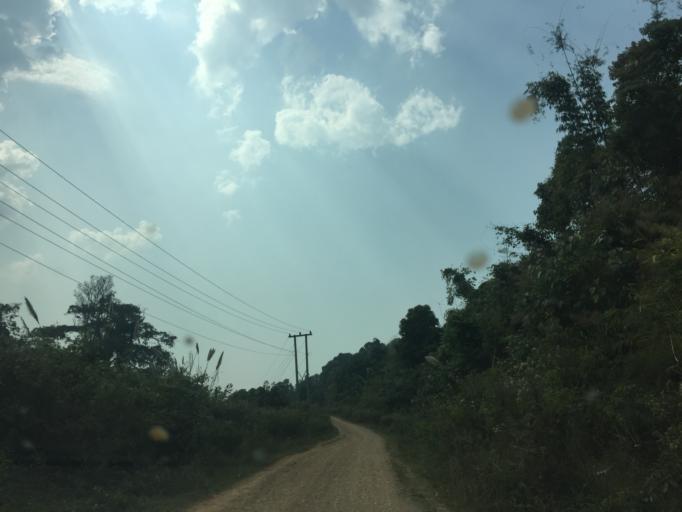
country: TH
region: Nan
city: Song Khwae
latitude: 19.7447
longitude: 100.7043
